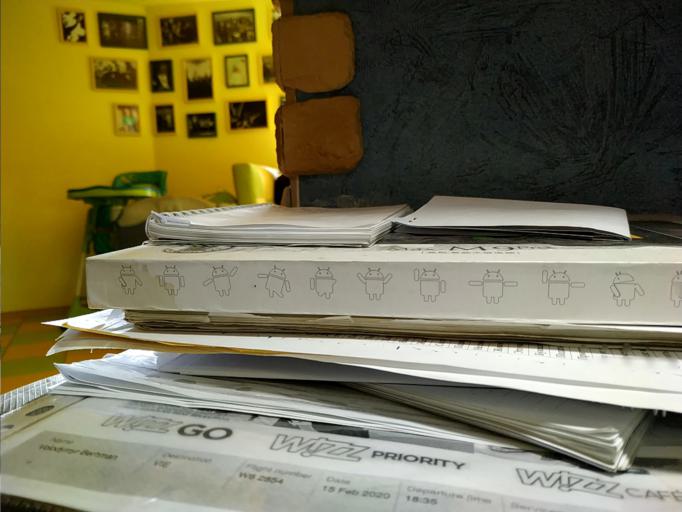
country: RU
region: Pskov
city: Plyussa
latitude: 58.5216
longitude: 29.5239
